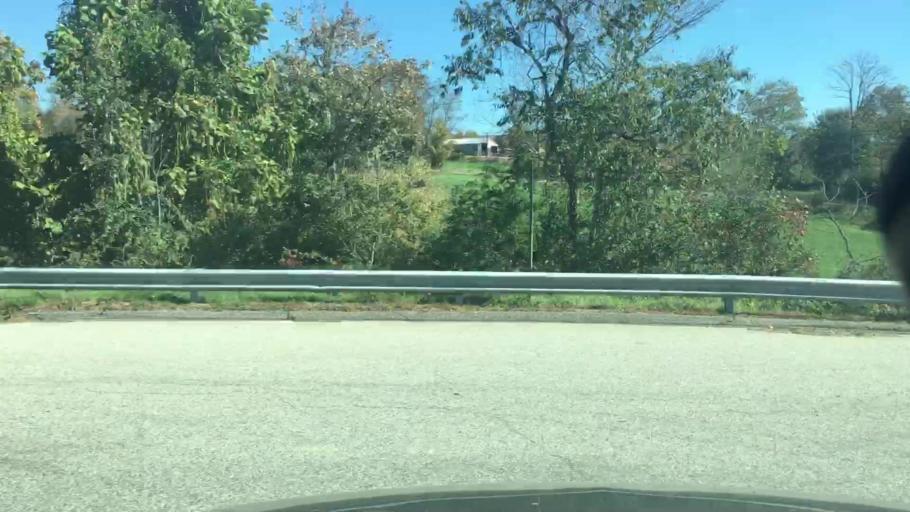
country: US
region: Connecticut
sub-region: Tolland County
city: Stafford
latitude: 41.9958
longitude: -72.2836
